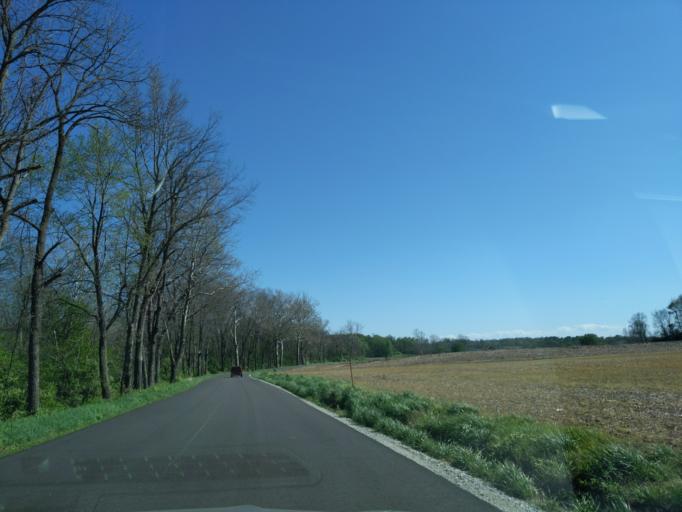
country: US
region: Indiana
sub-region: Decatur County
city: Greensburg
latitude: 39.2962
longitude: -85.4903
